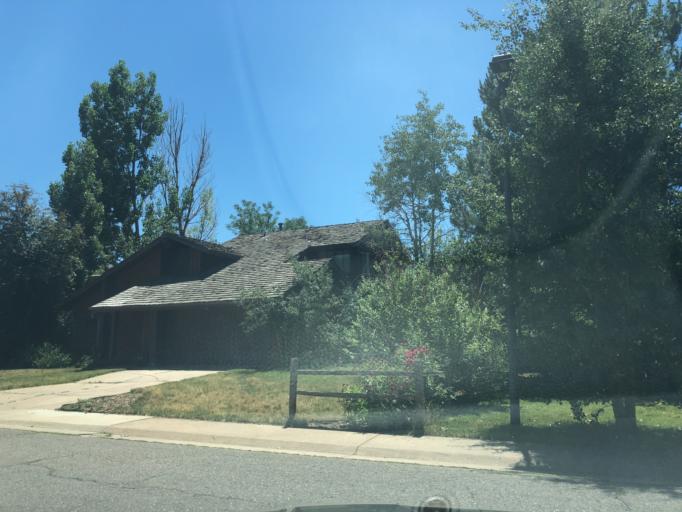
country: US
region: Colorado
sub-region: Arapahoe County
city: Dove Valley
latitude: 39.6158
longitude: -104.7747
